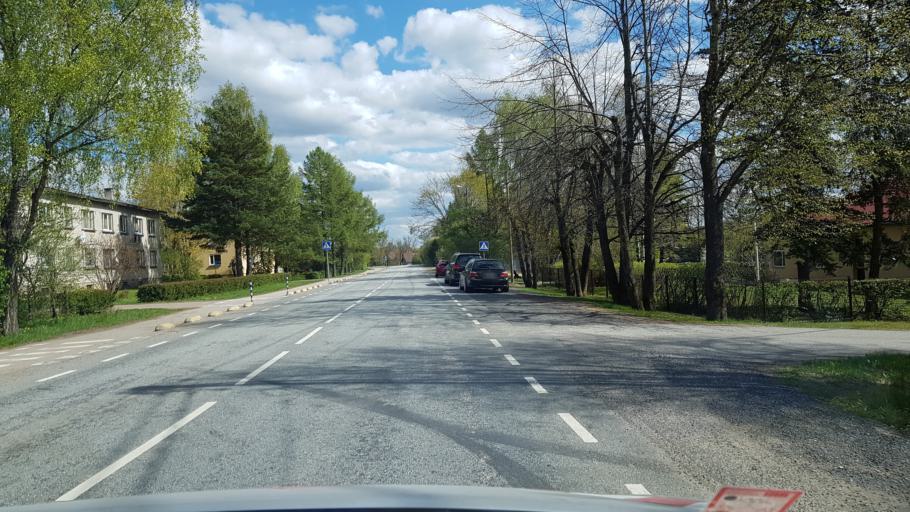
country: EE
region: Tartu
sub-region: UElenurme vald
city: Ulenurme
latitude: 58.2988
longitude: 26.8699
